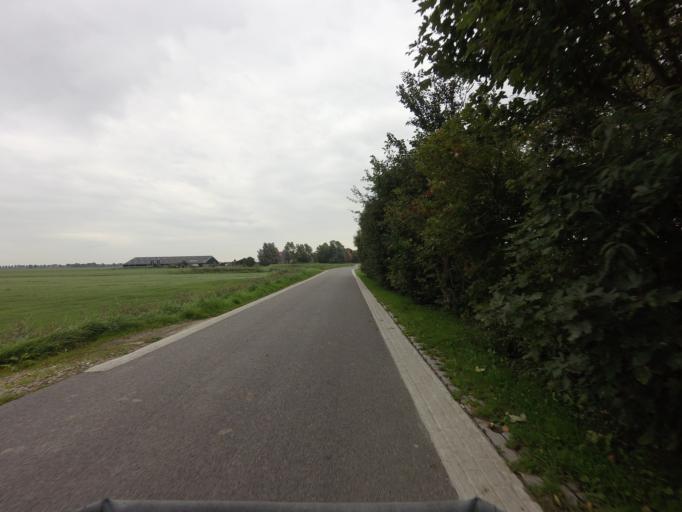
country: NL
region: Friesland
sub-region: Sudwest Fryslan
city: IJlst
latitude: 53.0109
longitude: 5.5791
